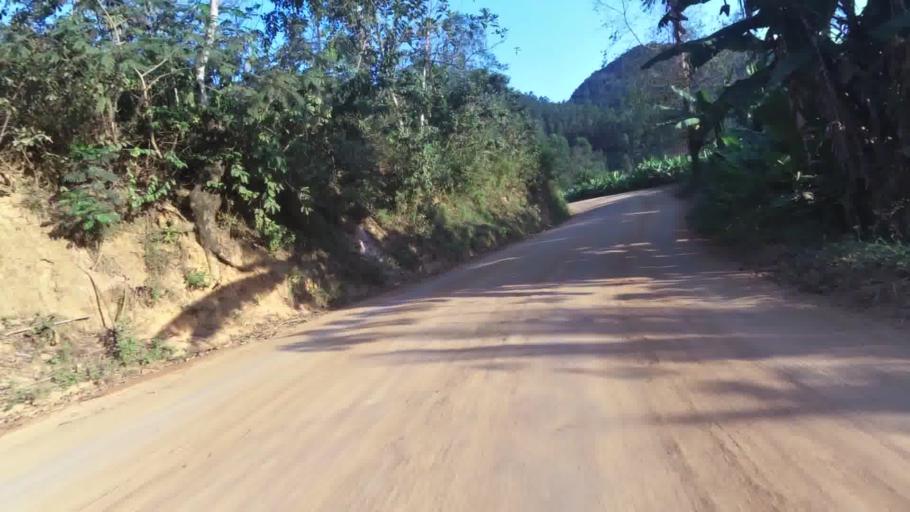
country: BR
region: Espirito Santo
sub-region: Alfredo Chaves
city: Alfredo Chaves
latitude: -20.5958
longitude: -40.6961
